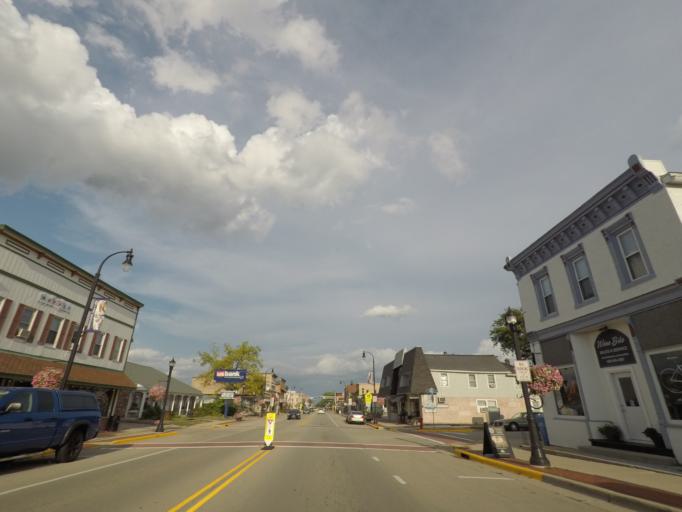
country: US
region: Wisconsin
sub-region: Dane County
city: Waunakee
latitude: 43.1919
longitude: -89.4572
